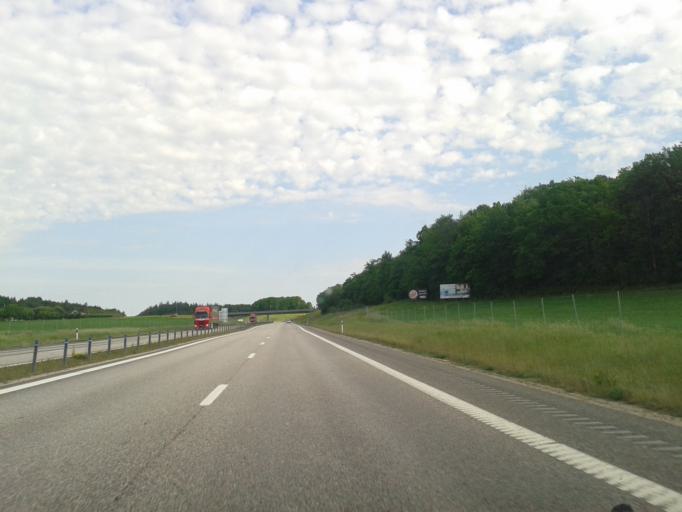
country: SE
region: Vaestra Goetaland
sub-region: Munkedals Kommun
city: Munkedal
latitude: 58.4652
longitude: 11.6533
